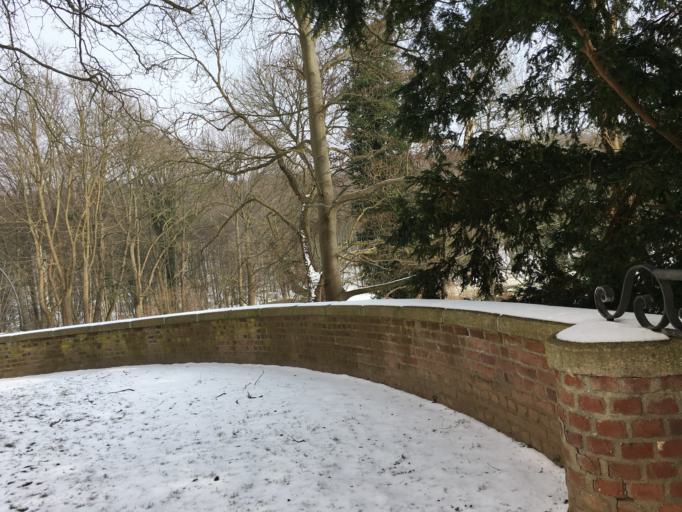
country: DE
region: North Rhine-Westphalia
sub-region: Regierungsbezirk Koln
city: Kreuzau
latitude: 50.7668
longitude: 6.5007
